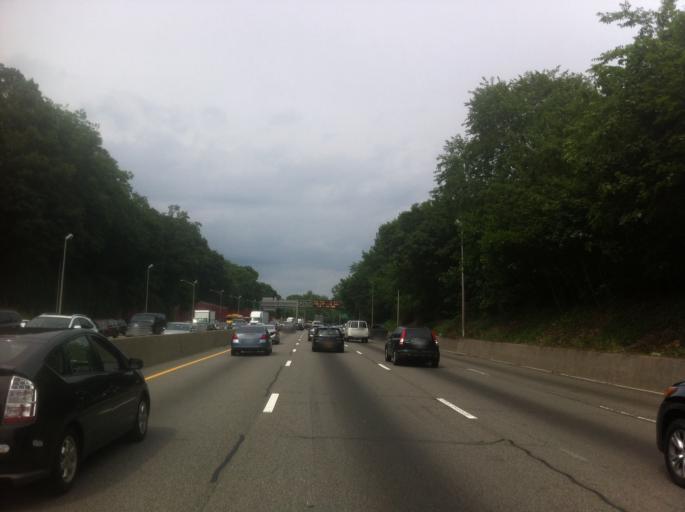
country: US
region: New York
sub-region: Nassau County
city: Lake Success
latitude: 40.7571
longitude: -73.7389
